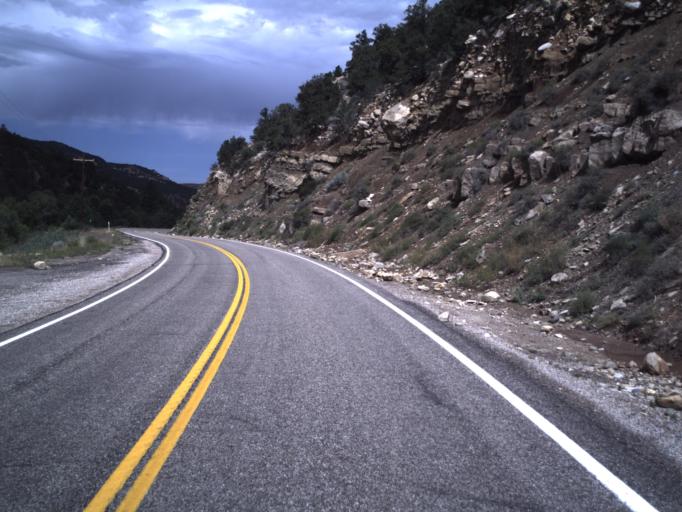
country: US
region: Utah
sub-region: Iron County
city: Cedar City
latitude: 37.6461
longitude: -112.9682
